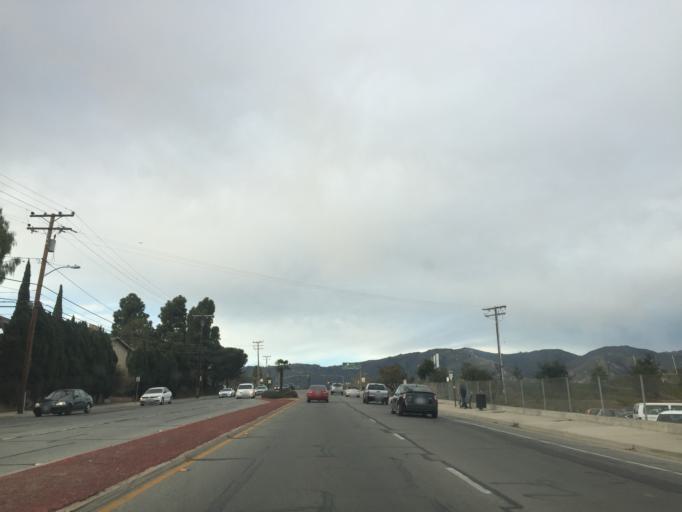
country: US
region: California
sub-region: Santa Barbara County
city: Goleta
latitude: 34.4391
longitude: -119.7893
